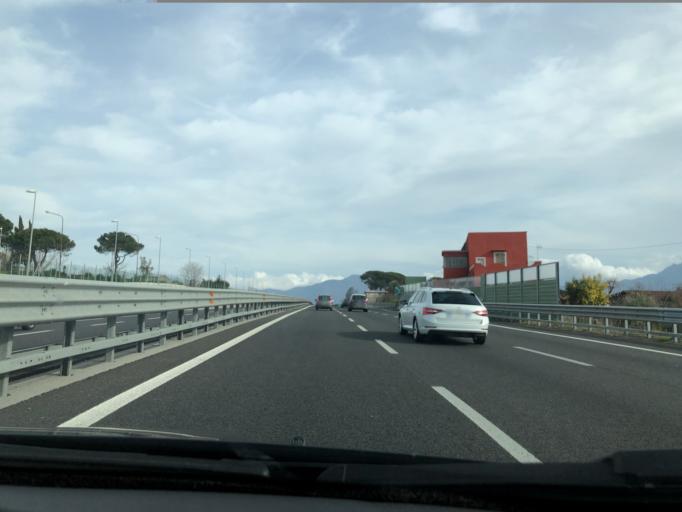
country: IT
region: Campania
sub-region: Provincia di Napoli
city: Torre del Greco
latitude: 40.7728
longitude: 14.4117
